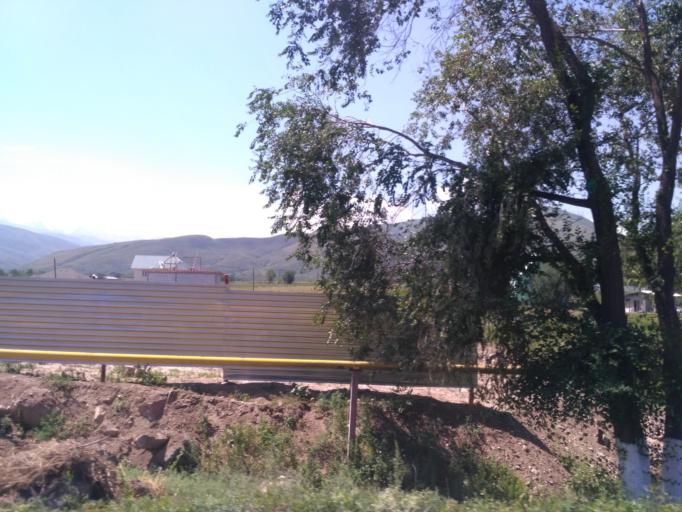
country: KZ
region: Almaty Oblysy
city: Burunday
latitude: 43.1663
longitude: 76.5991
